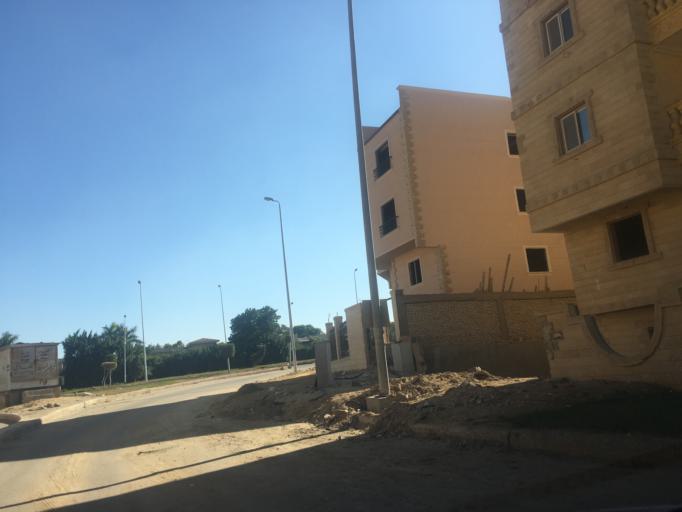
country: EG
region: Al Jizah
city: Awsim
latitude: 30.0256
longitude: 30.9851
